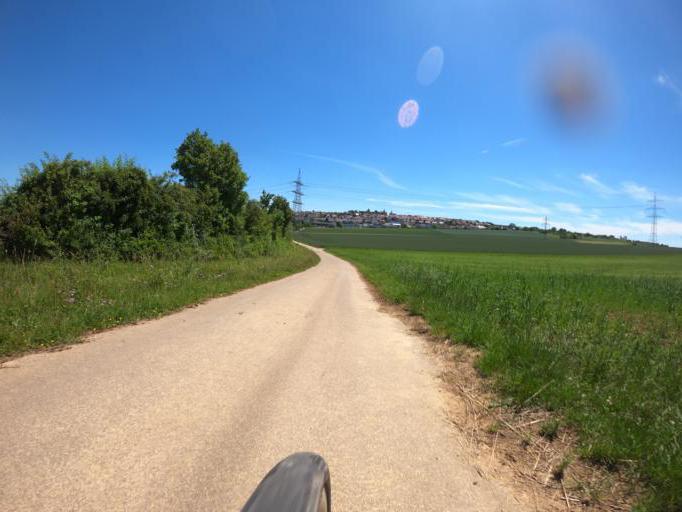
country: DE
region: Baden-Wuerttemberg
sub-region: Regierungsbezirk Stuttgart
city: Eberdingen
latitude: 48.9042
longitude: 8.9398
